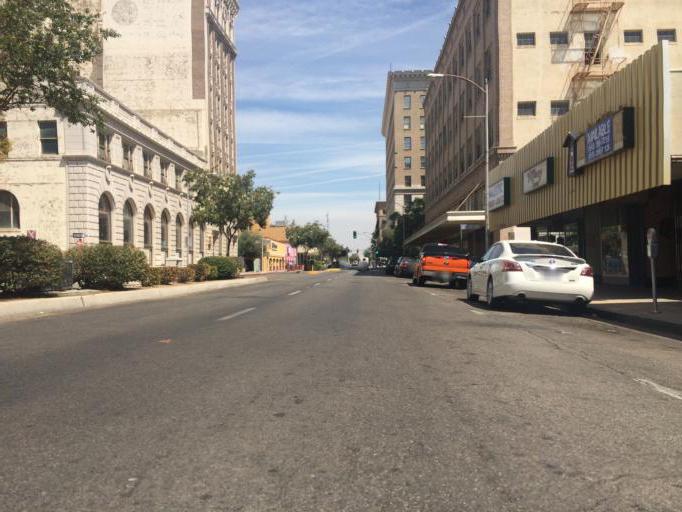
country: US
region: California
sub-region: Fresno County
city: Fresno
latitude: 36.7333
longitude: -119.7909
